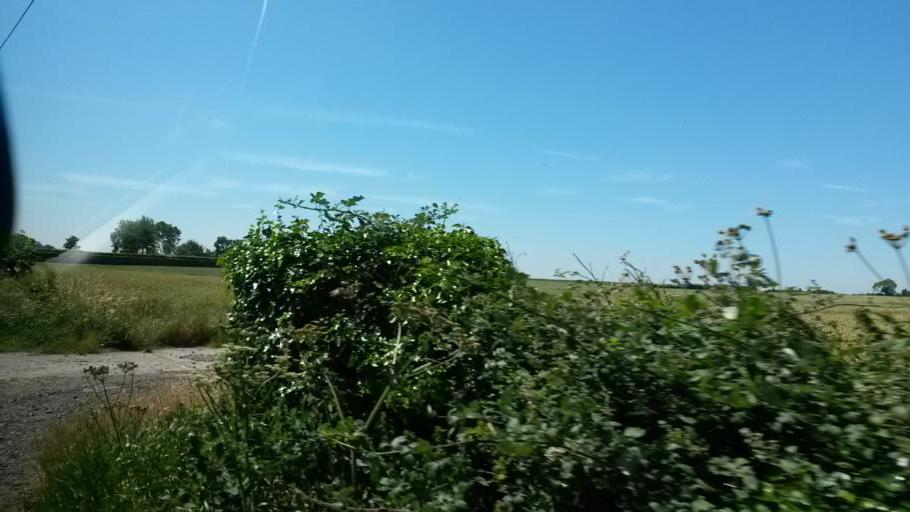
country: IE
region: Leinster
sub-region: Fingal County
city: Swords
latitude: 53.5015
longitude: -6.2696
